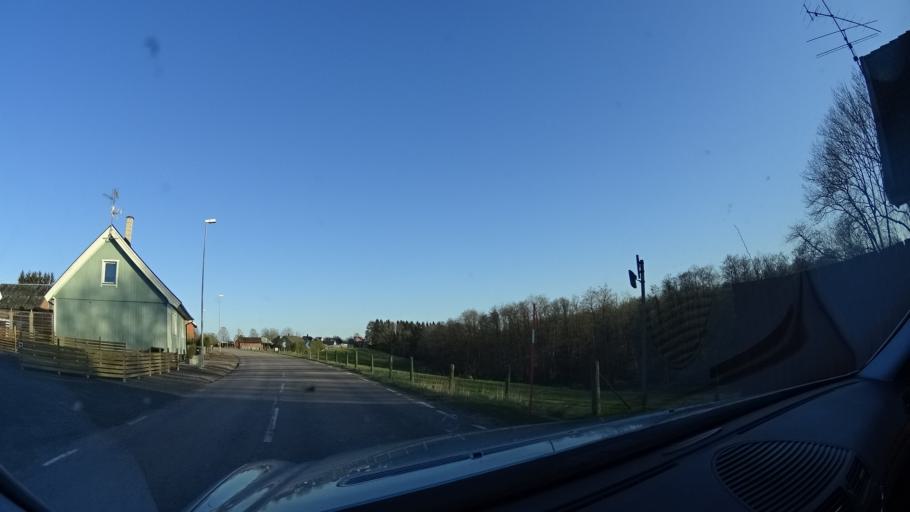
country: SE
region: Skane
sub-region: Bjuvs Kommun
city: Billesholm
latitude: 56.0548
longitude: 12.9960
